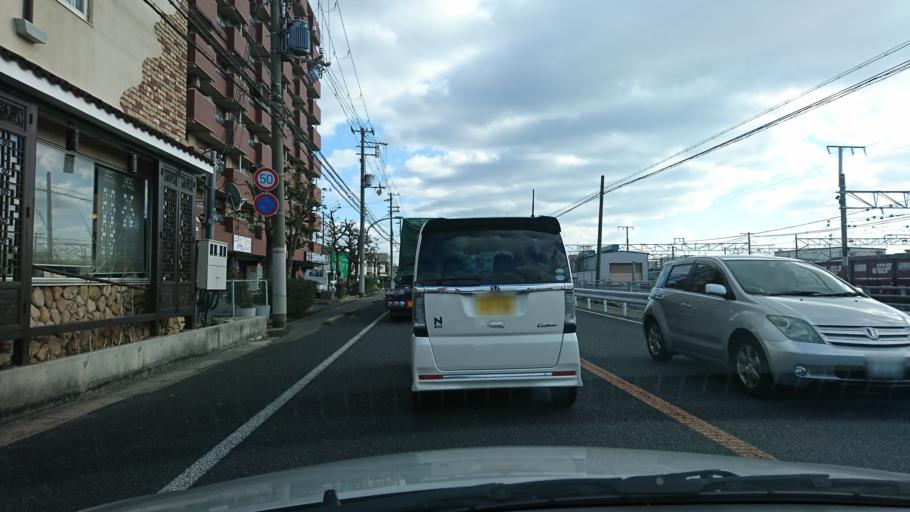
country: JP
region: Hyogo
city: Akashi
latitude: 34.6617
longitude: 134.9677
